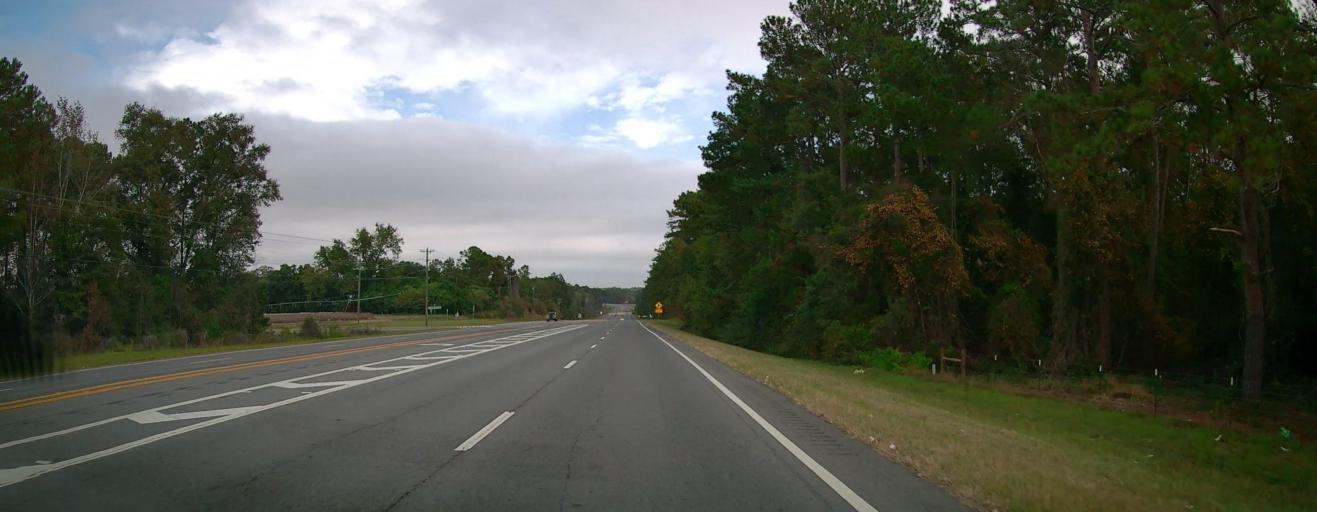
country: US
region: Georgia
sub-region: Tift County
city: Unionville
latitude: 31.3875
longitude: -83.5470
